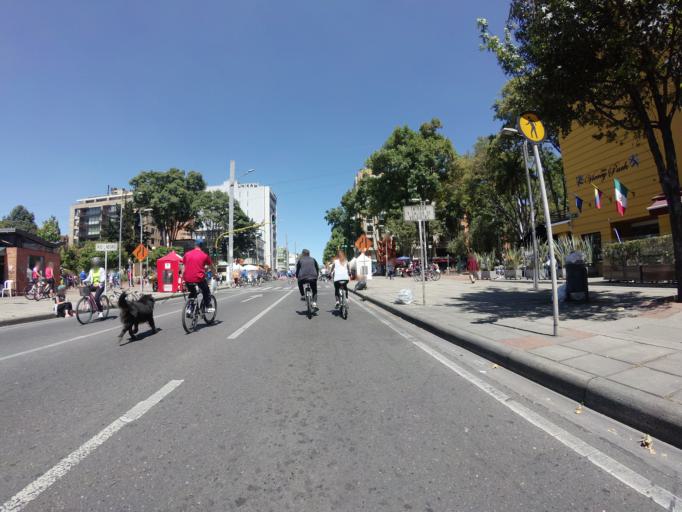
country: CO
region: Bogota D.C.
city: Barrio San Luis
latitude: 4.6728
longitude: -74.0540
